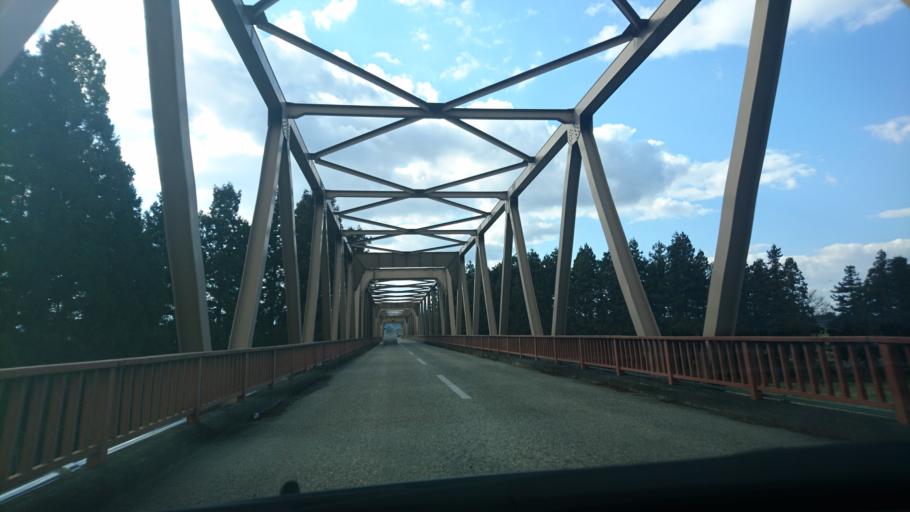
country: JP
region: Iwate
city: Mizusawa
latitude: 39.0412
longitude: 141.1463
